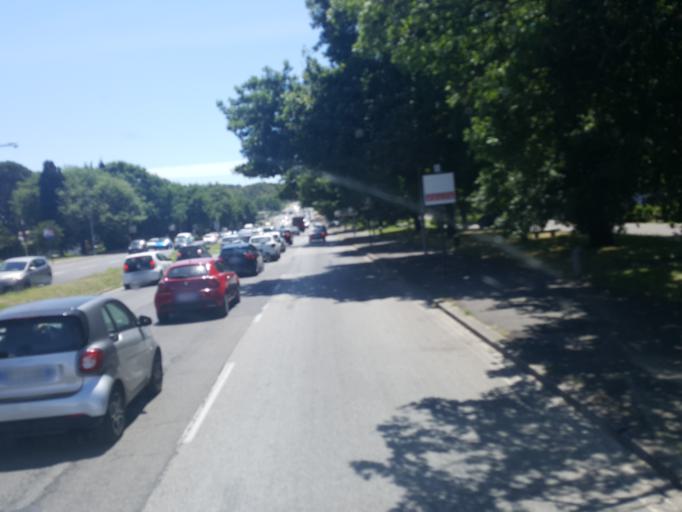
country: IT
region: Latium
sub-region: Citta metropolitana di Roma Capitale
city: Selcetta
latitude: 41.8218
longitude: 12.4646
